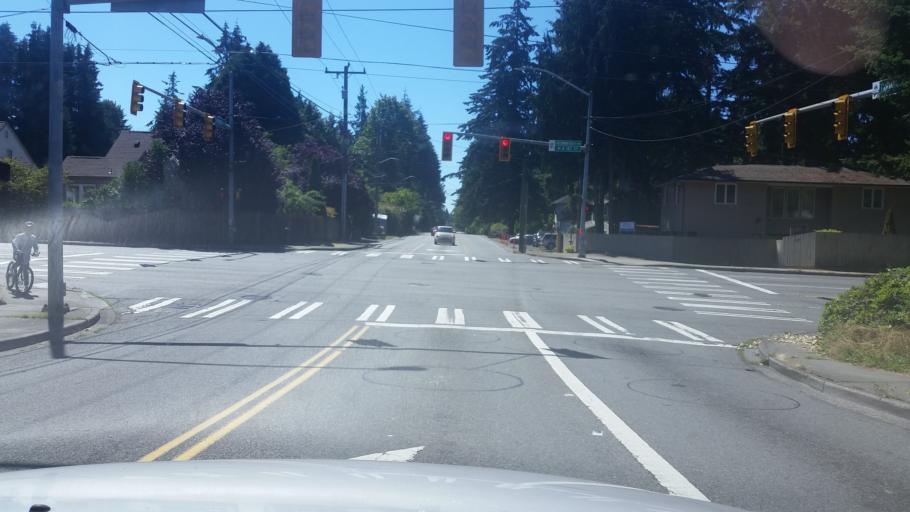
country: US
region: Washington
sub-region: King County
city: Shoreline
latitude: 47.7635
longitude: -122.3512
